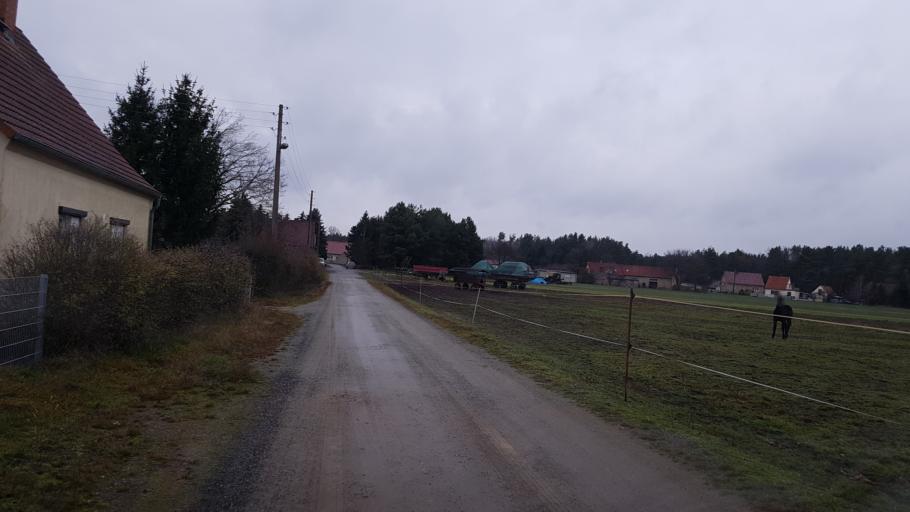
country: DE
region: Brandenburg
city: Altdobern
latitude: 51.6916
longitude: 14.0440
